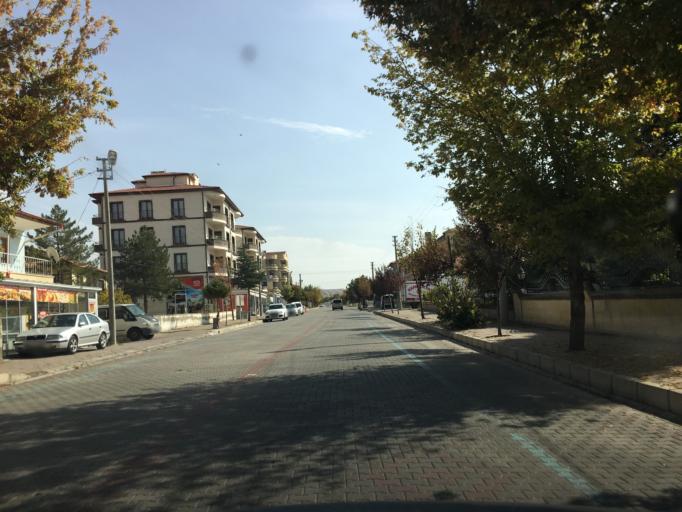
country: TR
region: Nevsehir
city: Avanos
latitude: 38.7082
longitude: 34.8512
